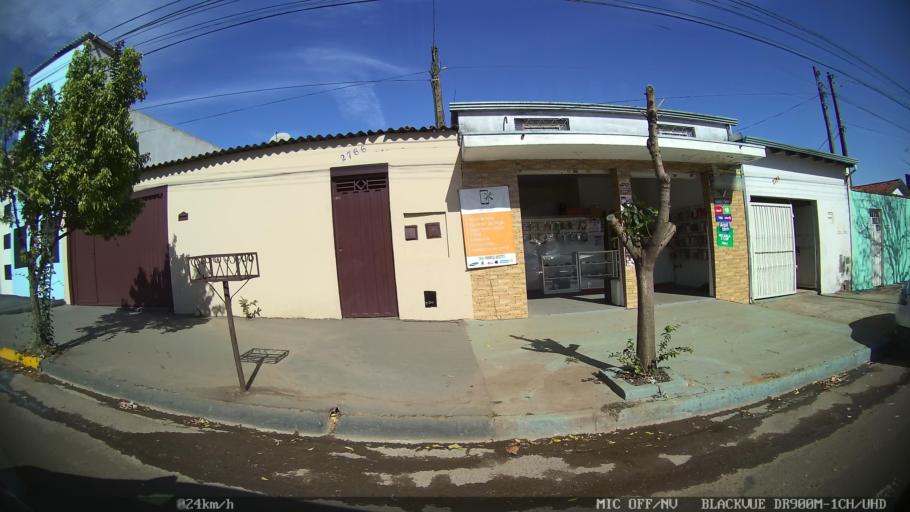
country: BR
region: Sao Paulo
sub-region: Franca
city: Franca
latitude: -20.5063
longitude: -47.4175
